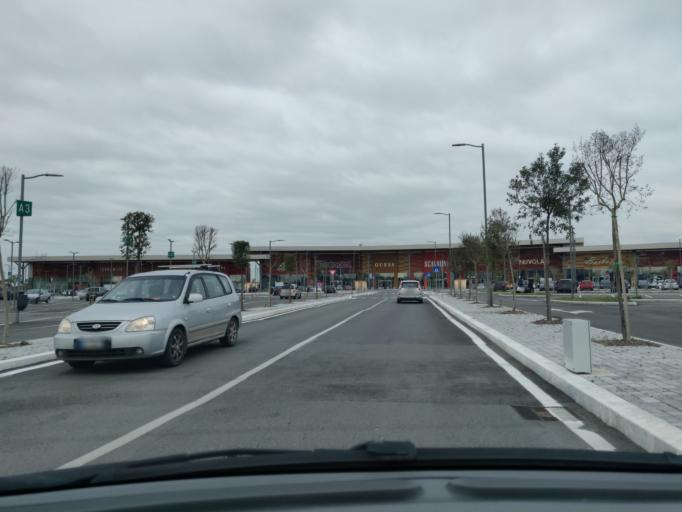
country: IT
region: Latium
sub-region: Citta metropolitana di Roma Capitale
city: Npp 23 (Parco Leonardo)
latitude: 41.8065
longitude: 12.2959
